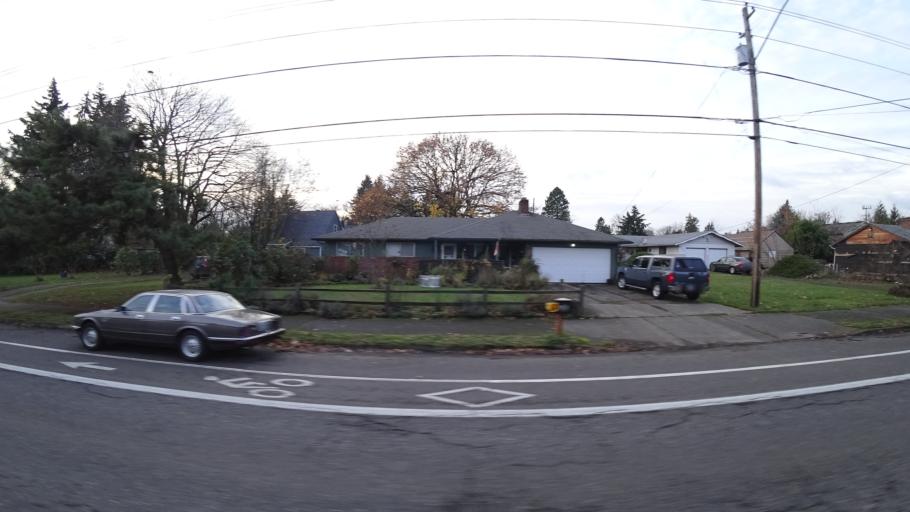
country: US
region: Oregon
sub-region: Multnomah County
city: Lents
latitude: 45.5160
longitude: -122.5107
